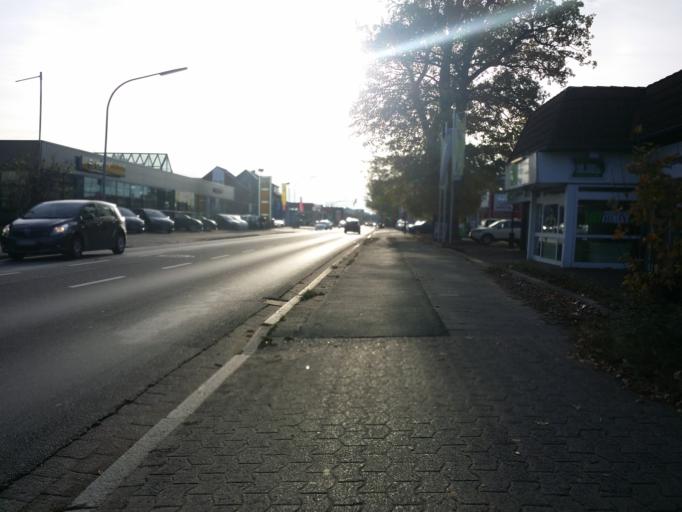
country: DE
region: Lower Saxony
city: Delmenhorst
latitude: 53.0357
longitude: 8.6486
